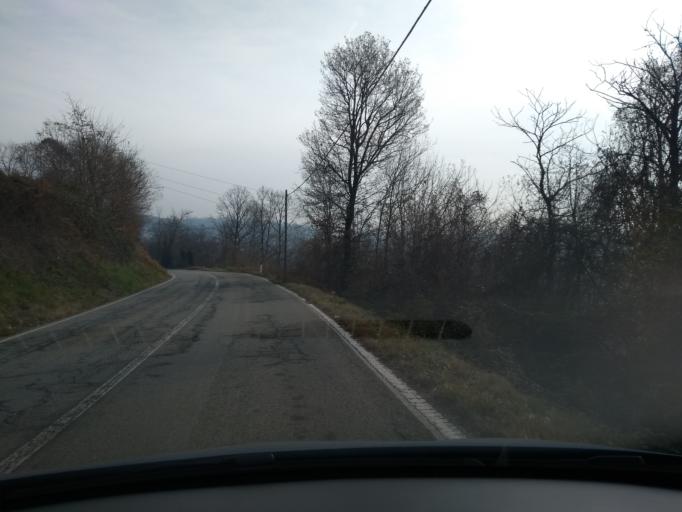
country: IT
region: Piedmont
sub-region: Provincia di Torino
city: Balangero
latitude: 45.2781
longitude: 7.5062
